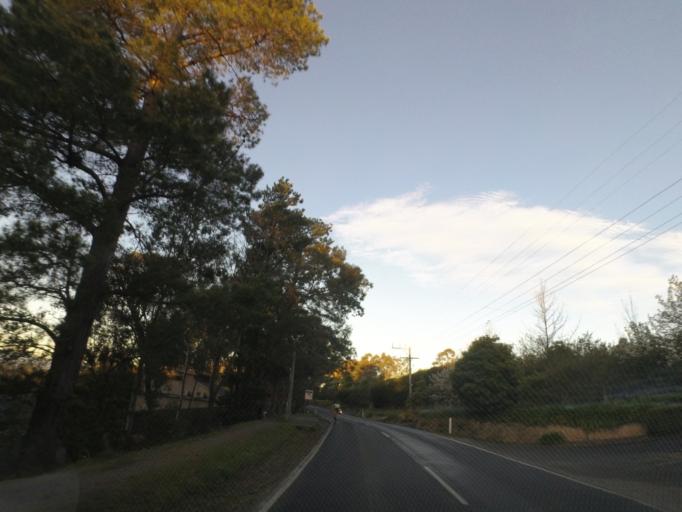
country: AU
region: Victoria
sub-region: Yarra Ranges
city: Chirnside Park
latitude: -37.7365
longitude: 145.2745
